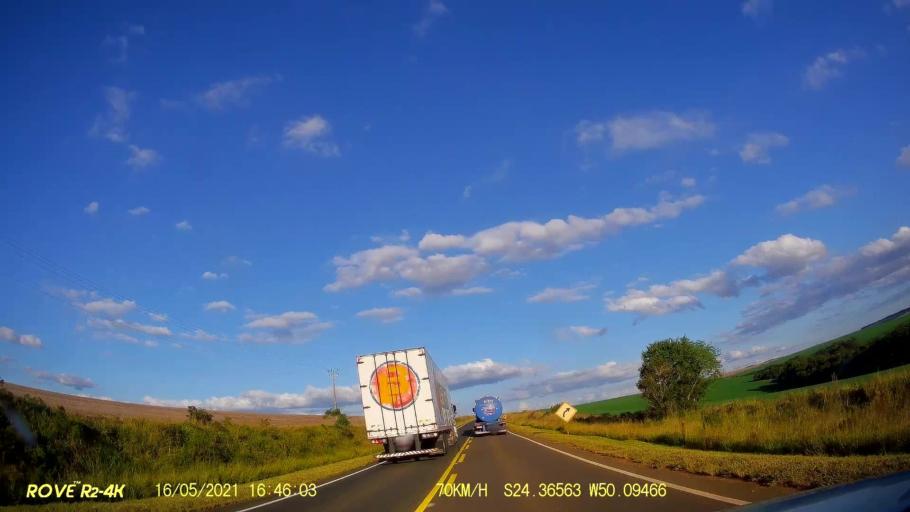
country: BR
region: Parana
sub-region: Pirai Do Sul
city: Pirai do Sul
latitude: -24.3659
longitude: -50.0946
